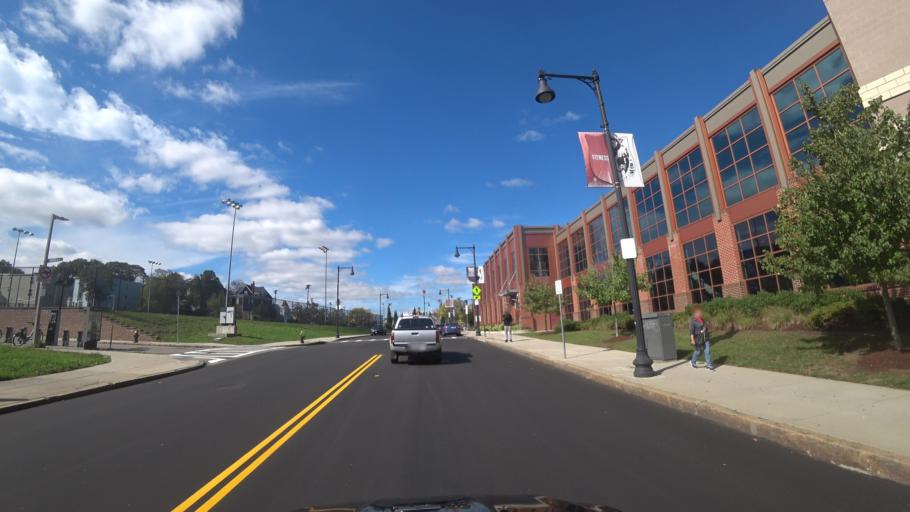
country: US
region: Massachusetts
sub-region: Suffolk County
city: South Boston
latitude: 42.3188
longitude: -71.0693
